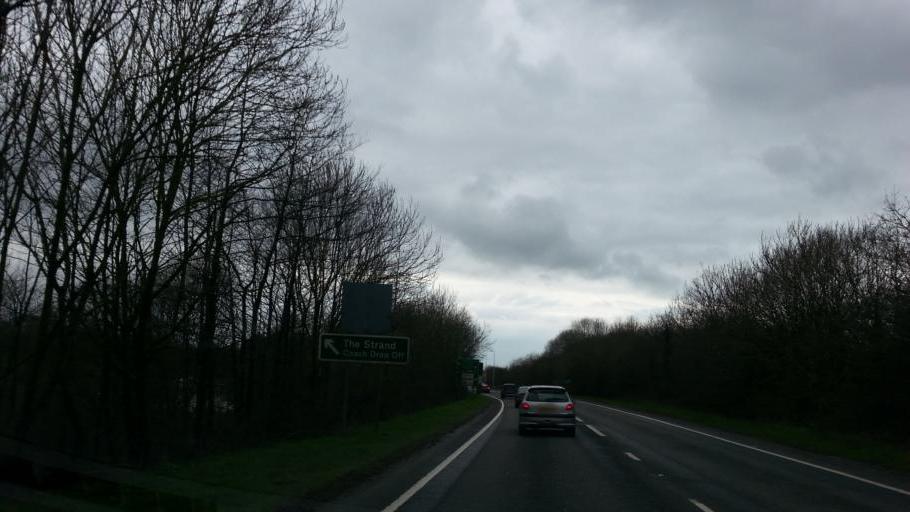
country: GB
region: England
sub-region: Devon
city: Barnstaple
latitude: 51.0714
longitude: -4.0277
